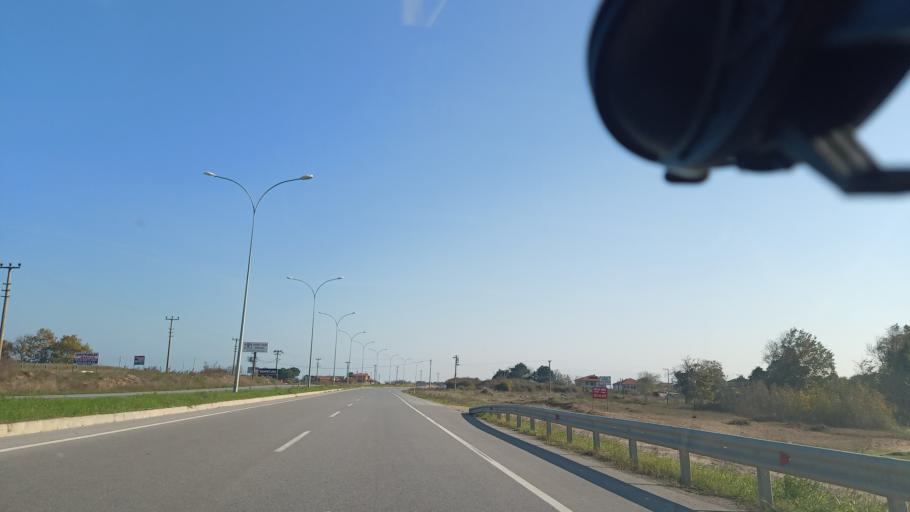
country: TR
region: Sakarya
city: Karasu
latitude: 41.0872
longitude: 30.7459
